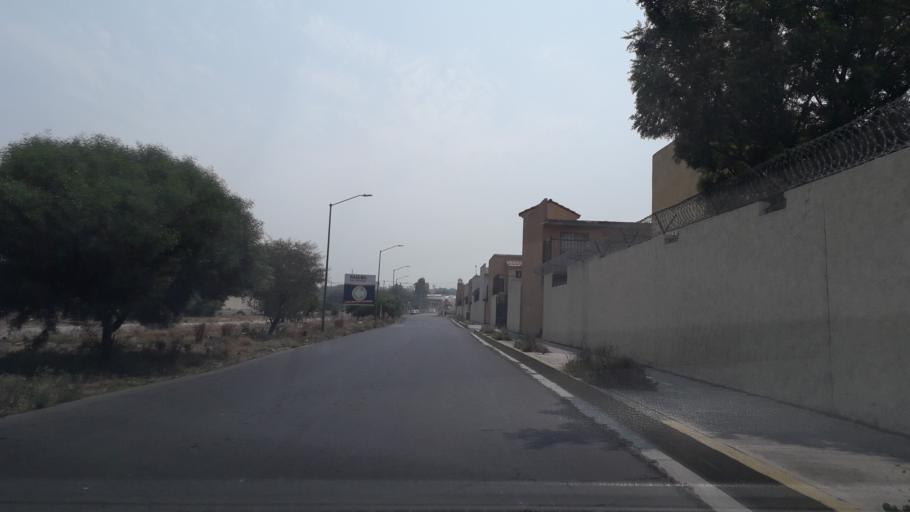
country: MX
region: Mexico
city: Santo Tomas Chiconautla
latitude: 19.6512
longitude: -99.0209
